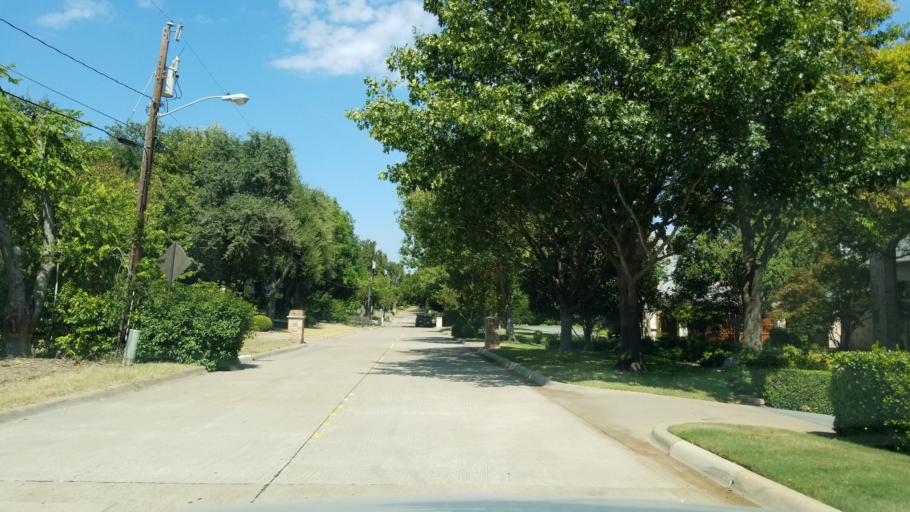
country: US
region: Texas
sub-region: Dallas County
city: Addison
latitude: 32.9473
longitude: -96.8105
